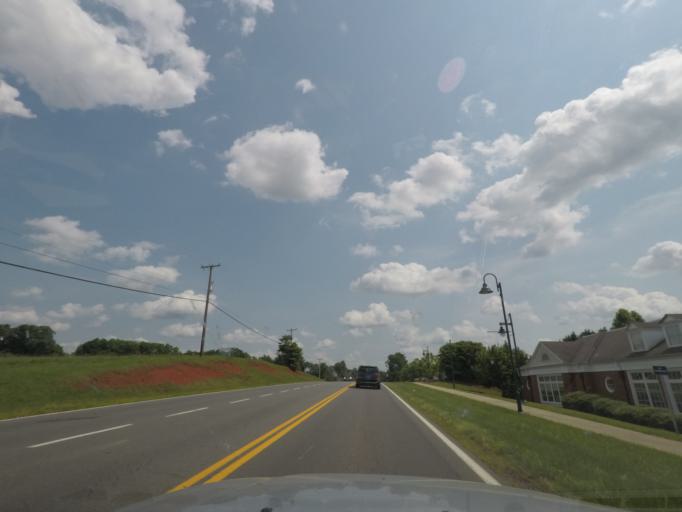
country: US
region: Virginia
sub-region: Orange County
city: Orange
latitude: 38.2599
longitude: -78.1168
